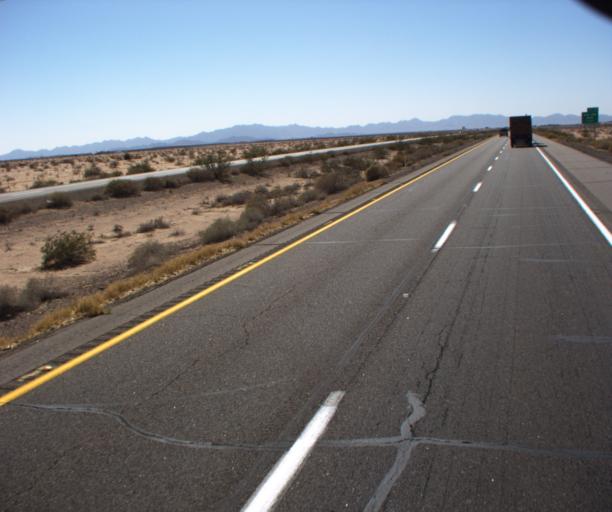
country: US
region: Arizona
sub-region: Yuma County
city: Wellton
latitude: 32.6866
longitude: -113.9988
